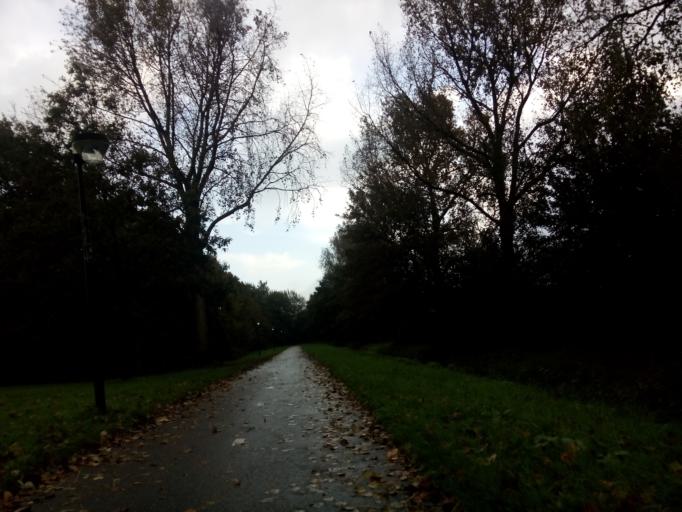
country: NL
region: South Holland
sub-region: Gemeente Maassluis
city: Maassluis
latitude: 51.9228
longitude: 4.2703
